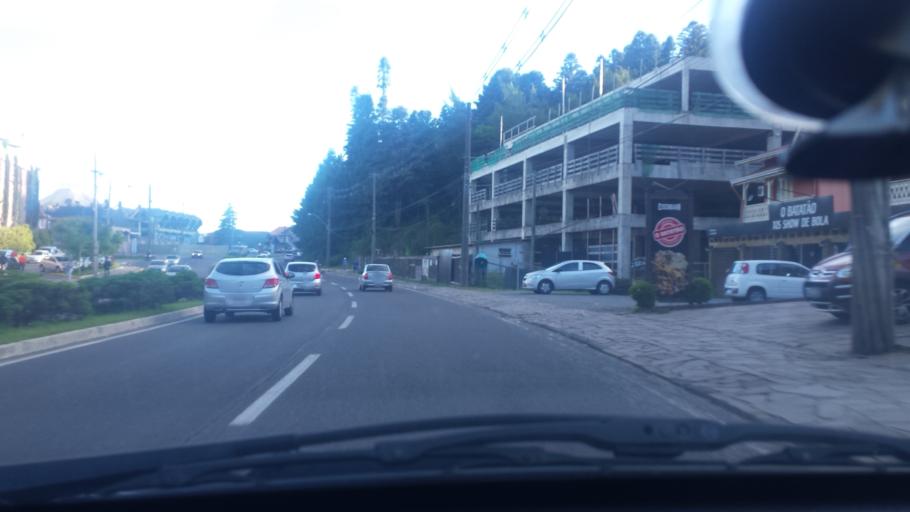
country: BR
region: Rio Grande do Sul
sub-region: Canela
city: Canela
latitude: -29.3745
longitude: -50.8649
